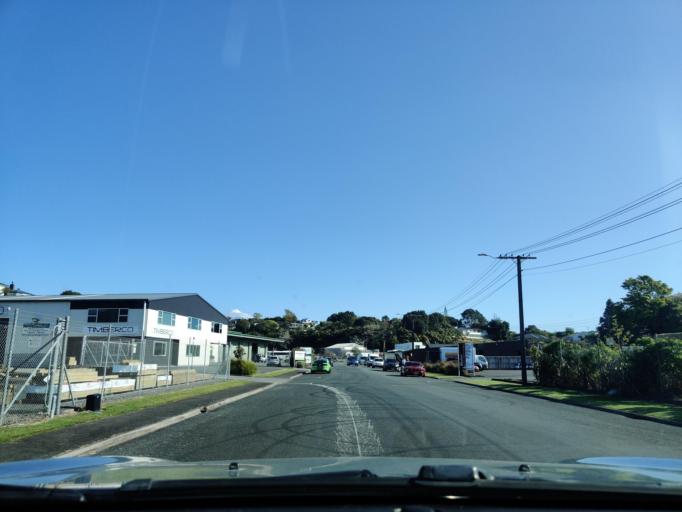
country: NZ
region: Taranaki
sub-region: New Plymouth District
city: New Plymouth
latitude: -39.0763
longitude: 174.0546
